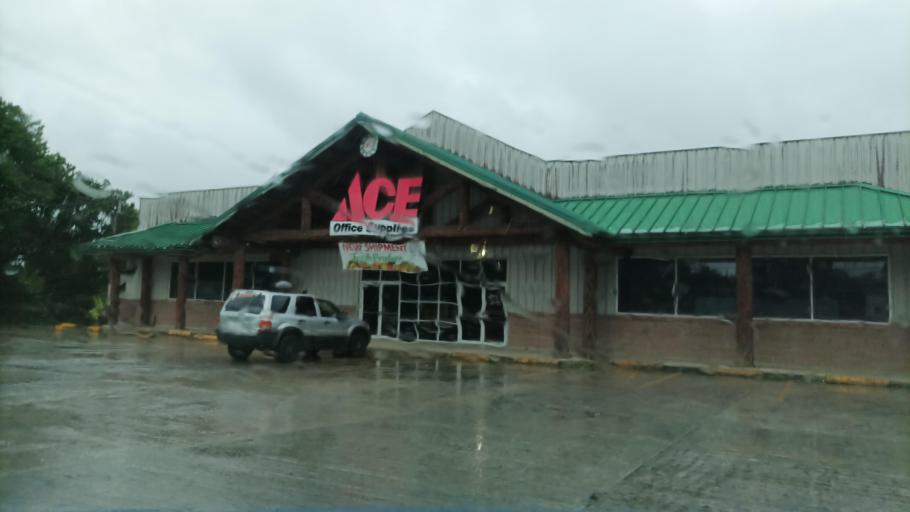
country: FM
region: Pohnpei
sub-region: Kolonia Municipality
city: Kolonia
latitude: 6.9601
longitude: 158.2151
